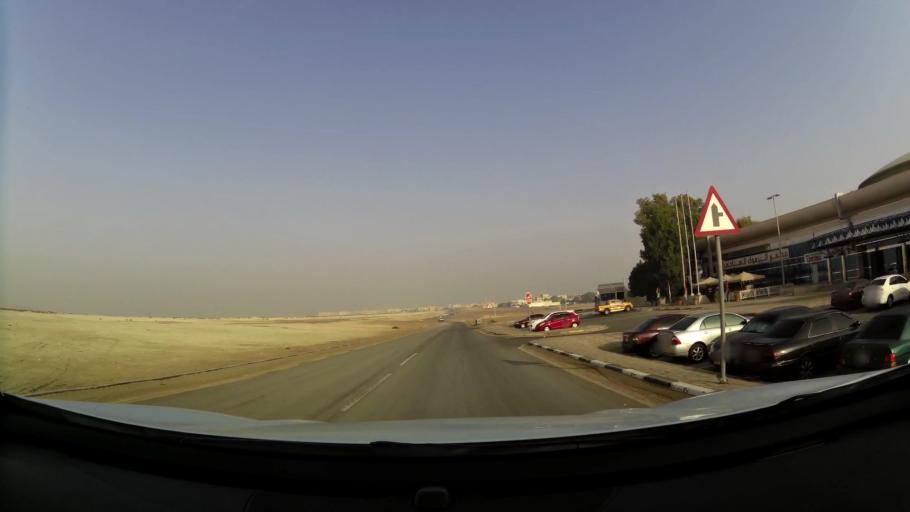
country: AE
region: Abu Dhabi
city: Abu Dhabi
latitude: 24.2811
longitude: 54.6420
